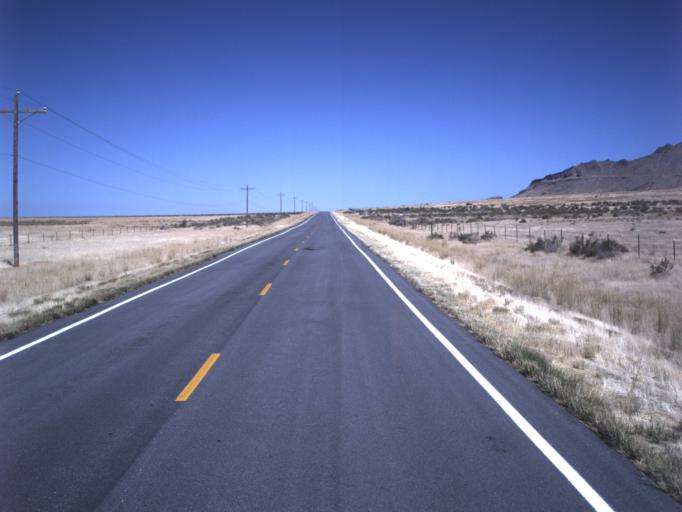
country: US
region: Utah
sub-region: Tooele County
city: Grantsville
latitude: 40.6891
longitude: -112.6689
